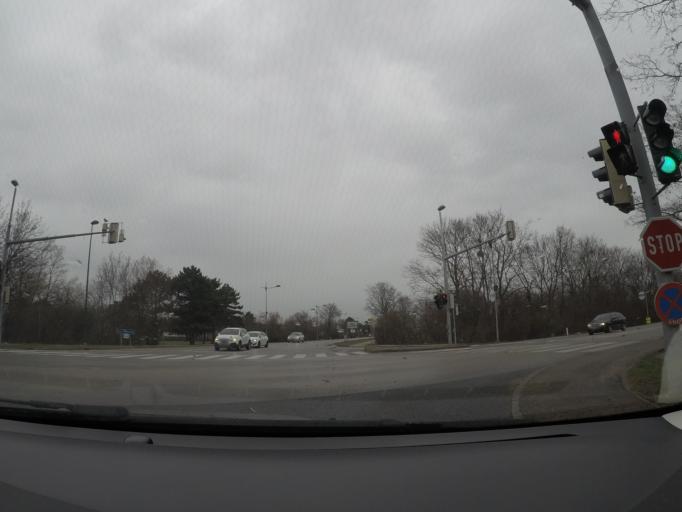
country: AT
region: Lower Austria
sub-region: Politischer Bezirk Modling
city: Wiener Neudorf
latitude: 48.0914
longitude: 16.3105
